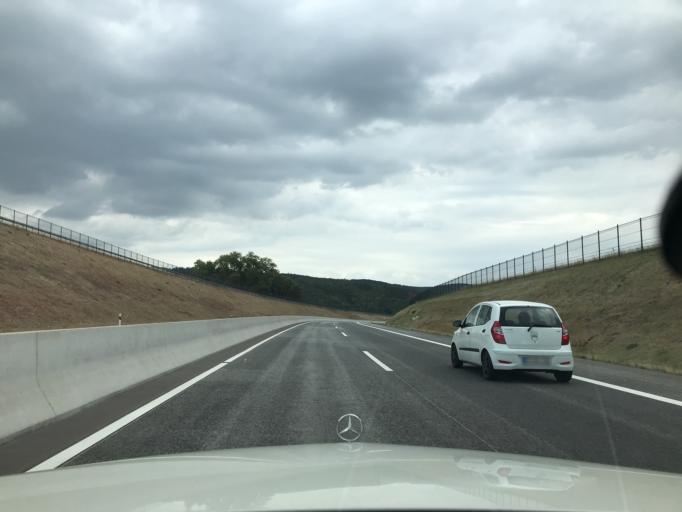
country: DE
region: Hesse
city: Waldkappel
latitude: 51.1552
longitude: 9.8826
